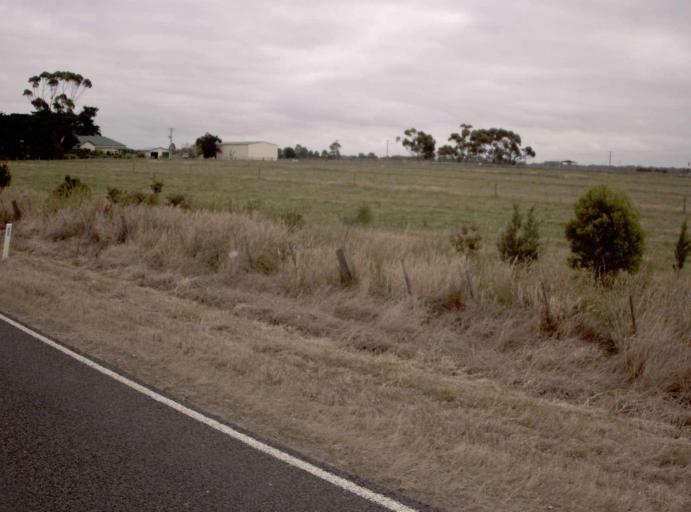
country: AU
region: Victoria
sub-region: Wellington
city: Sale
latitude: -38.0732
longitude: 146.9831
